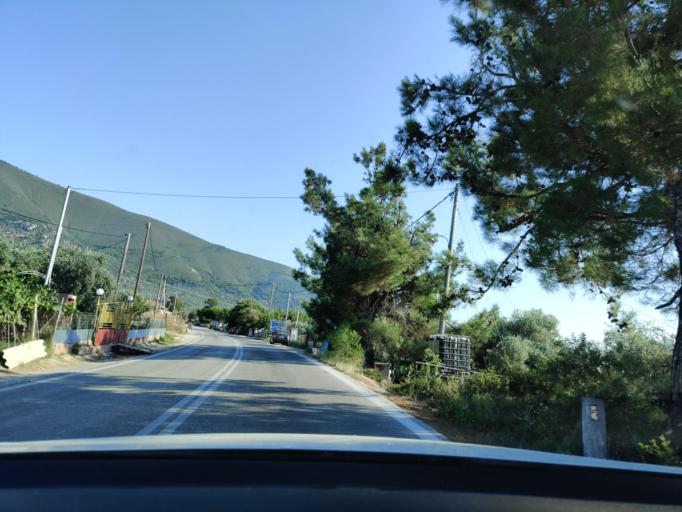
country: GR
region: East Macedonia and Thrace
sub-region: Nomos Kavalas
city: Prinos
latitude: 40.6950
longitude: 24.5251
